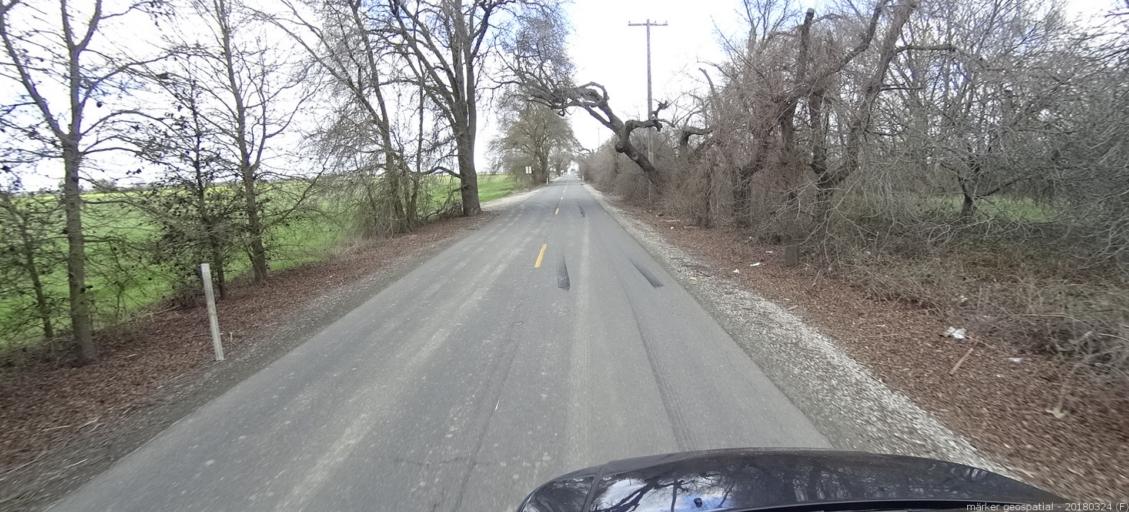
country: US
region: California
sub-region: Yolo County
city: West Sacramento
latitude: 38.6530
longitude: -121.5766
